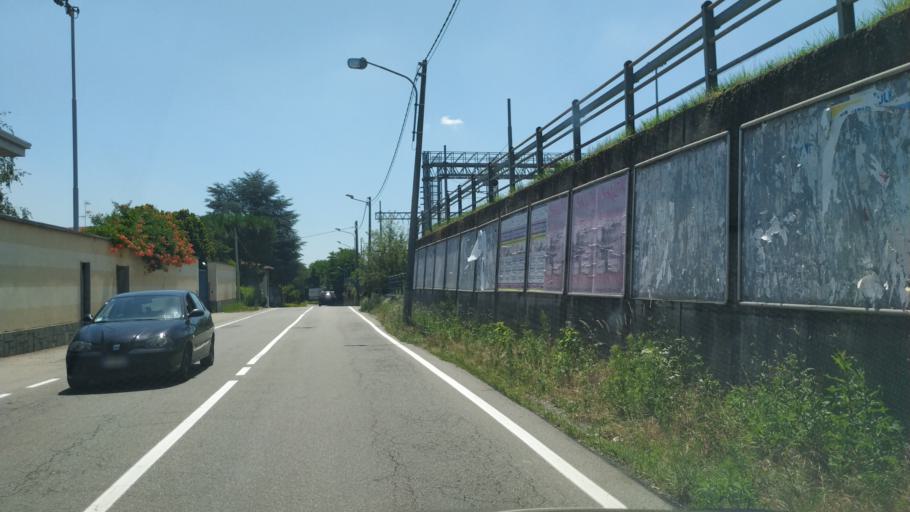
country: IT
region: Piedmont
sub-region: Provincia di Novara
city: Borgomanero
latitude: 45.6985
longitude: 8.4701
